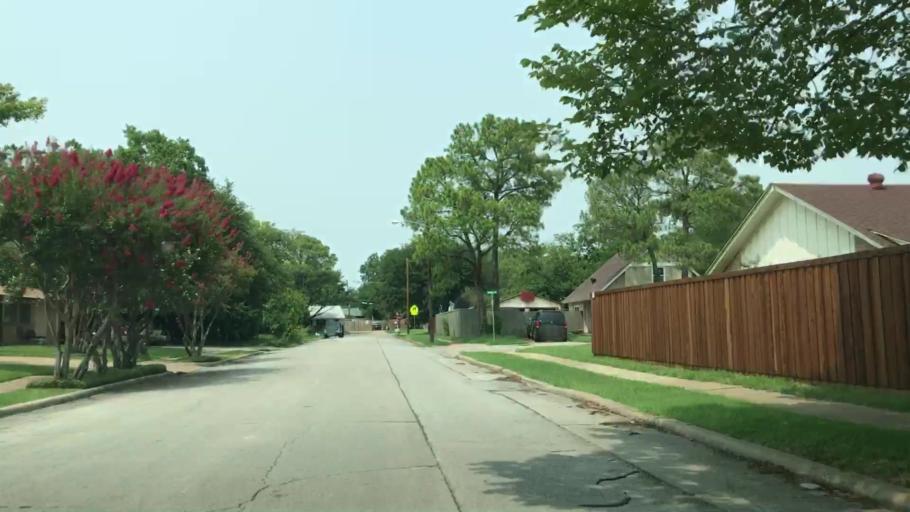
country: US
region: Texas
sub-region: Dallas County
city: Irving
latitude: 32.8500
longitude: -96.9648
